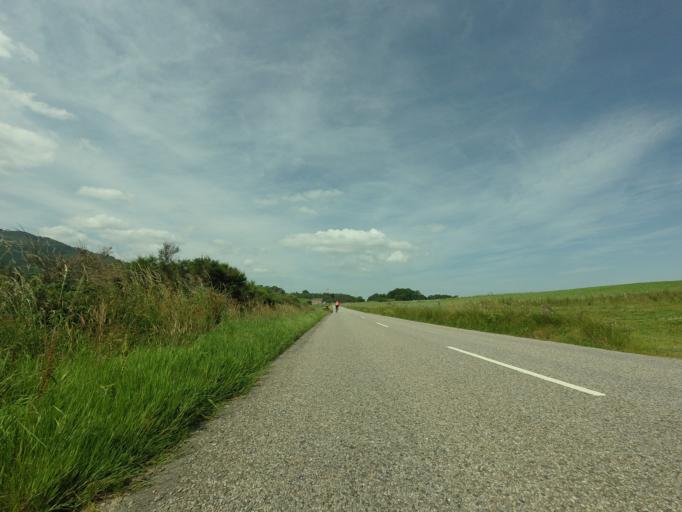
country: GB
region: Scotland
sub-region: Highland
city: Tain
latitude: 57.8465
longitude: -4.2001
